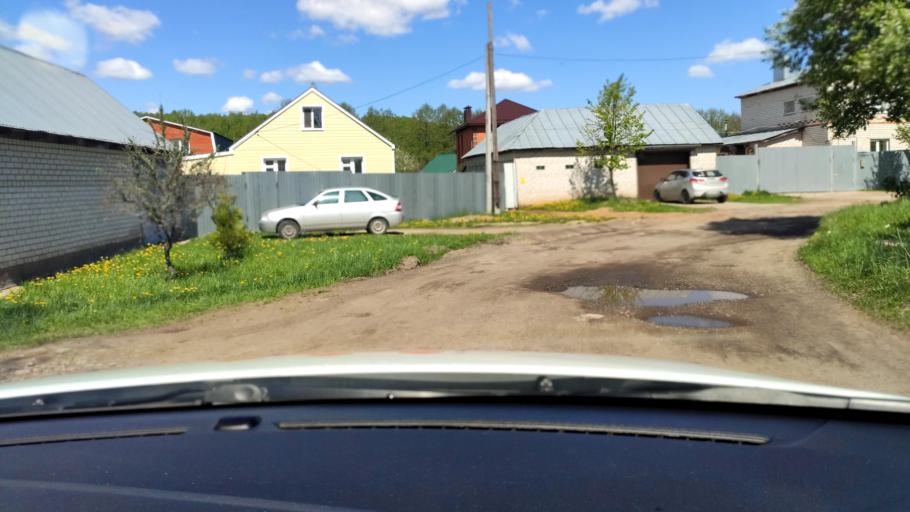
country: RU
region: Tatarstan
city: Vysokaya Gora
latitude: 55.8187
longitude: 49.2770
